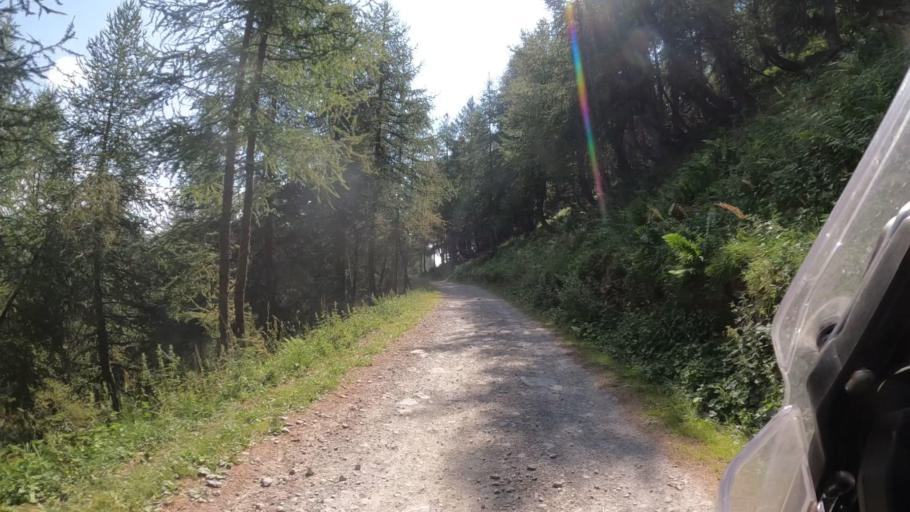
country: IT
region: Piedmont
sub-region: Provincia di Cuneo
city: Briga Alta
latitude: 44.0881
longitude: 7.7233
